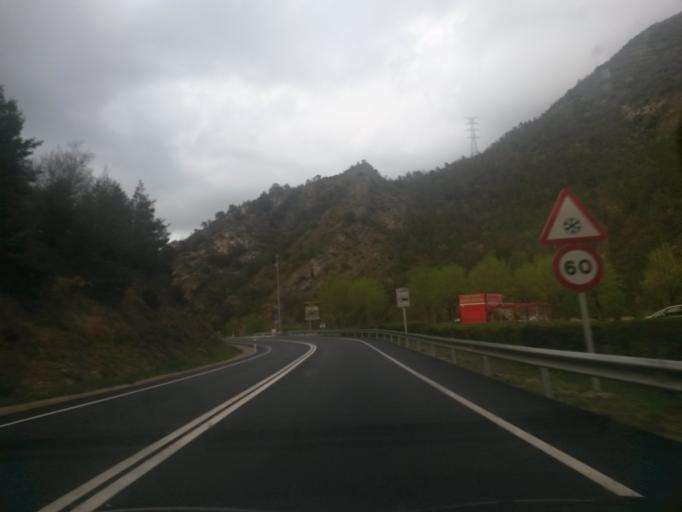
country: ES
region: Catalonia
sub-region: Provincia de Barcelona
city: Guardiola de Bergueda
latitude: 42.2123
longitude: 1.8692
